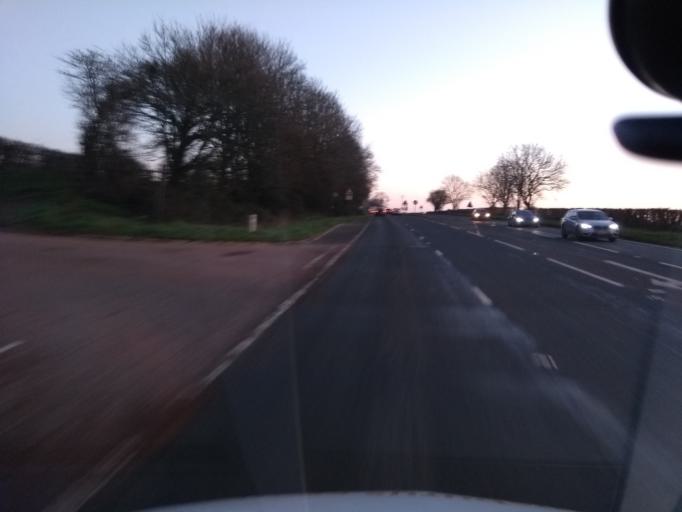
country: GB
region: England
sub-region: Somerset
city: North Petherton
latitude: 51.0656
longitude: -3.0260
